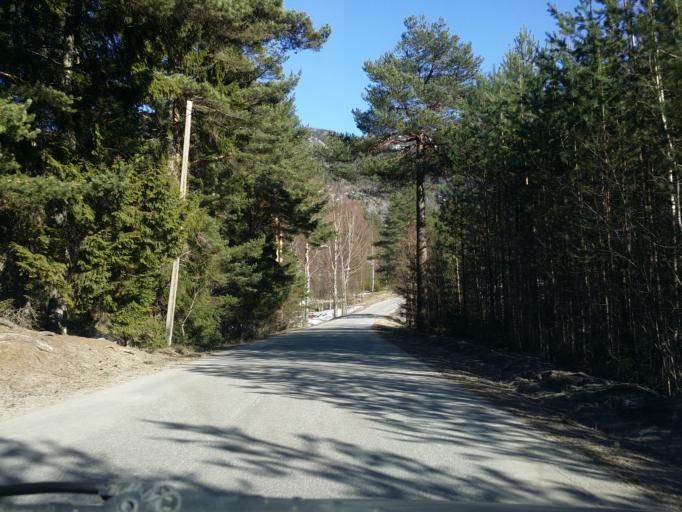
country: NO
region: Buskerud
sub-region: Ringerike
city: Honefoss
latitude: 60.3540
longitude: 10.0875
